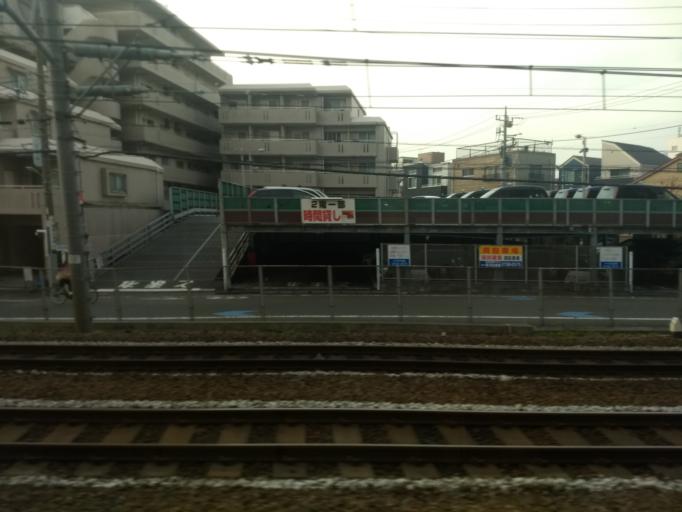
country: JP
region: Kanagawa
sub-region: Kawasaki-shi
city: Kawasaki
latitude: 35.5560
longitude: 139.7133
